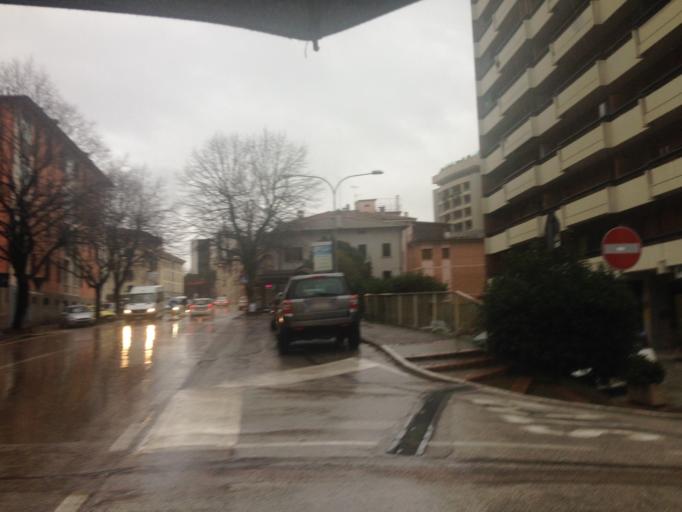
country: IT
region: Umbria
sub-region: Provincia di Perugia
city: Perugia
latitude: 43.1061
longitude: 12.3712
